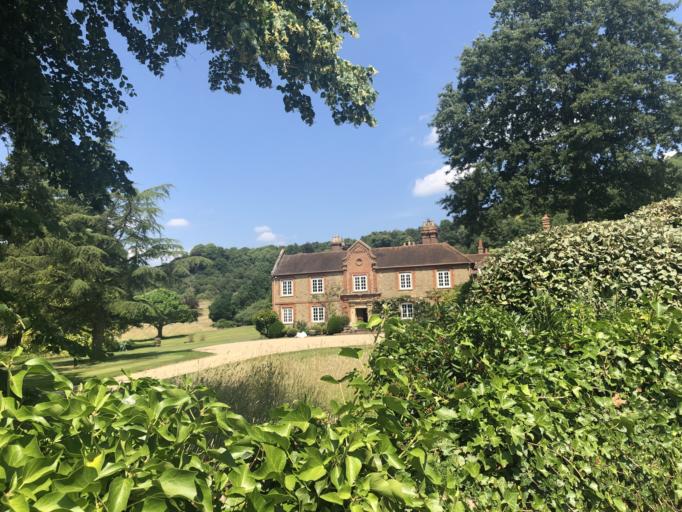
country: GB
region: England
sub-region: Surrey
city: Chilworth
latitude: 51.2199
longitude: -0.5307
